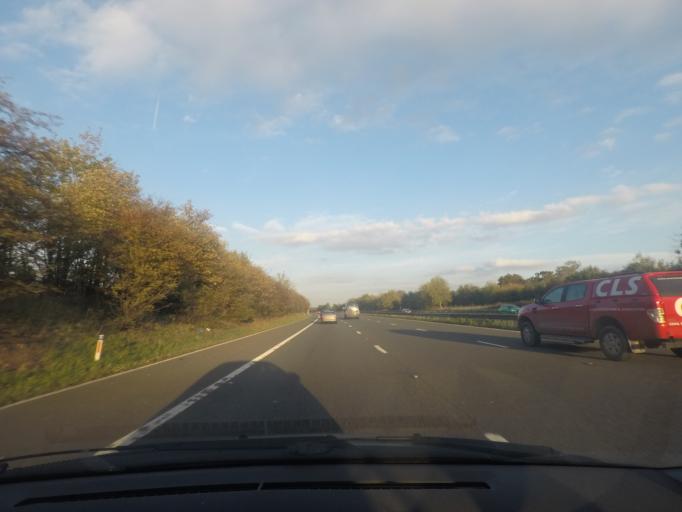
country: GB
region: England
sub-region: North Lincolnshire
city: Scawby
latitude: 53.5453
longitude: -0.5447
